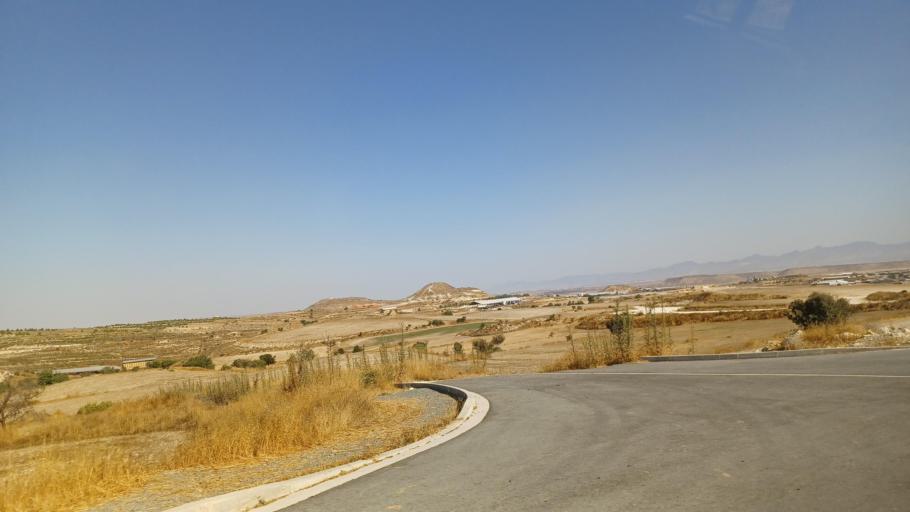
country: CY
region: Larnaka
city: Athienou
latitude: 35.0264
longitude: 33.5475
